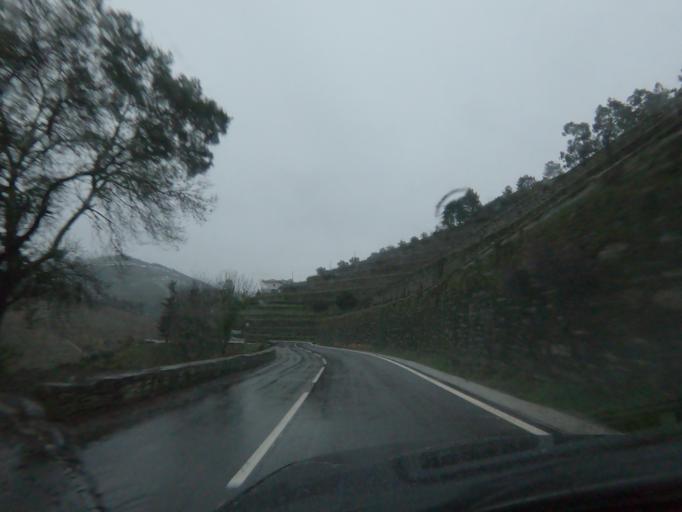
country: PT
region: Vila Real
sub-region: Sabrosa
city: Vilela
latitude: 41.1985
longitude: -7.5574
